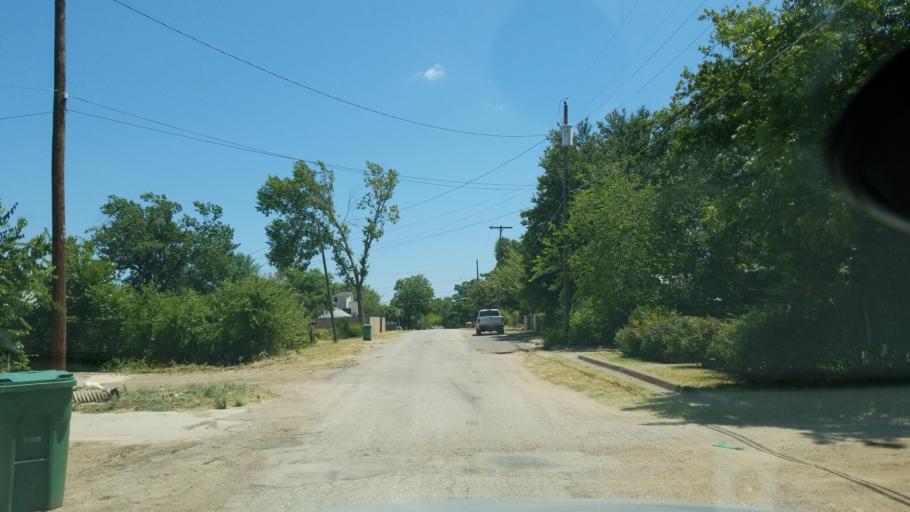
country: US
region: Texas
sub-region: Dallas County
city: Cockrell Hill
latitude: 32.7375
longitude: -96.8824
